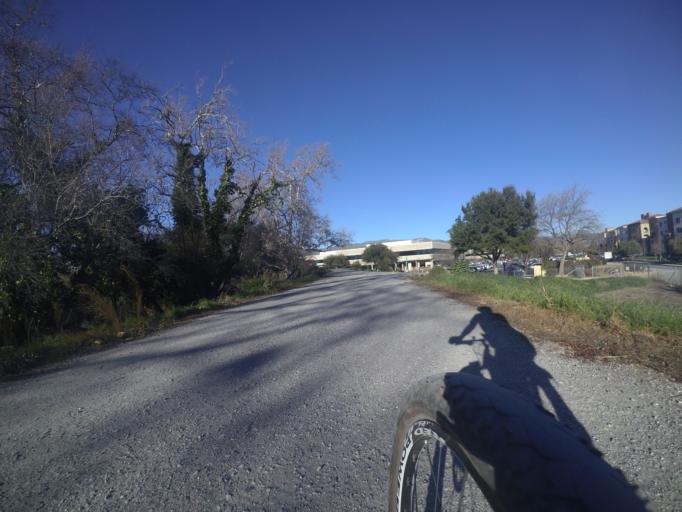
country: US
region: California
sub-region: Santa Clara County
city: Milpitas
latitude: 37.4183
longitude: -121.9299
